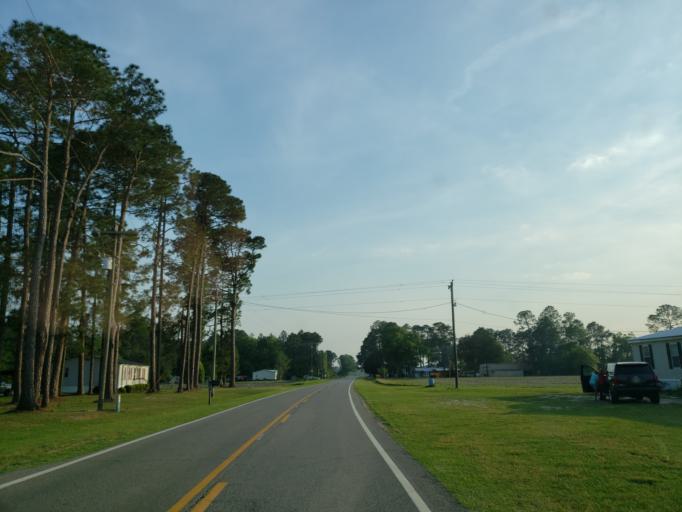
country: US
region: Georgia
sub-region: Cook County
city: Sparks
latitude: 31.2025
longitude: -83.4231
